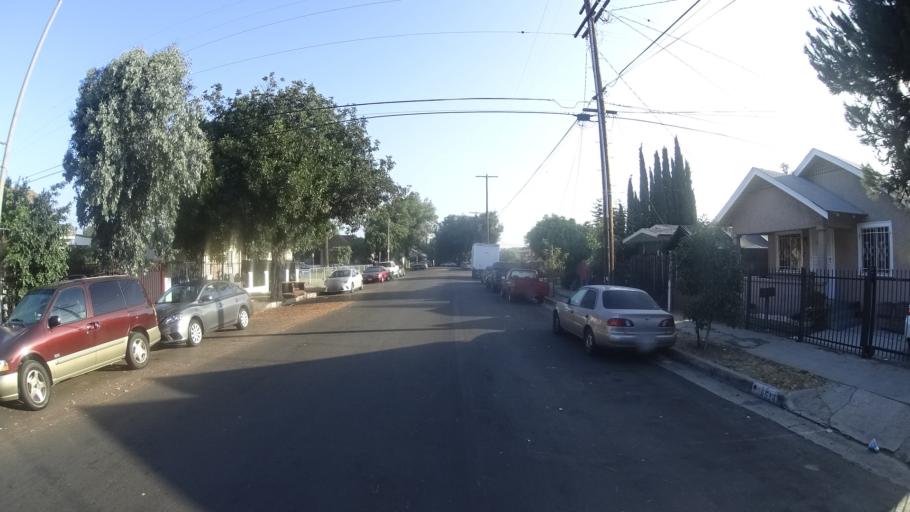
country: US
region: California
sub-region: Los Angeles County
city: Westmont
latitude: 33.9795
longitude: -118.2893
